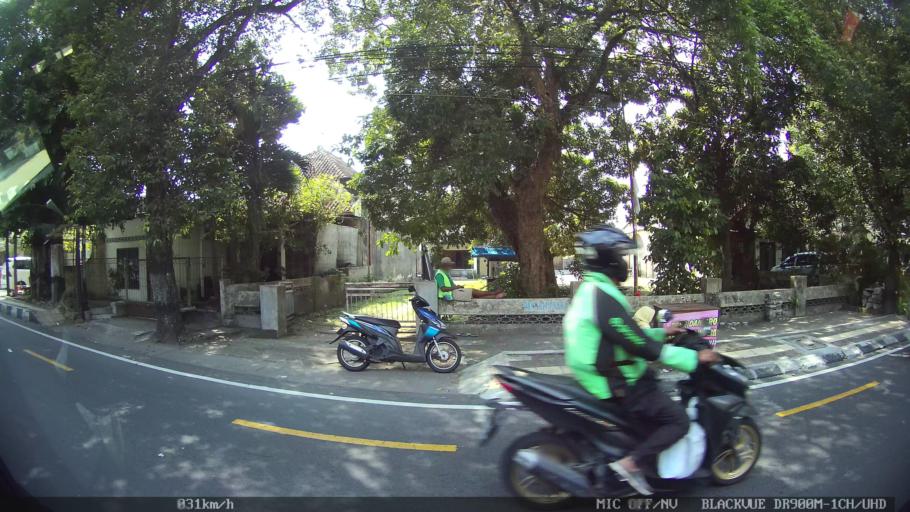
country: ID
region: Daerah Istimewa Yogyakarta
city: Yogyakarta
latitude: -7.8030
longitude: 110.3950
